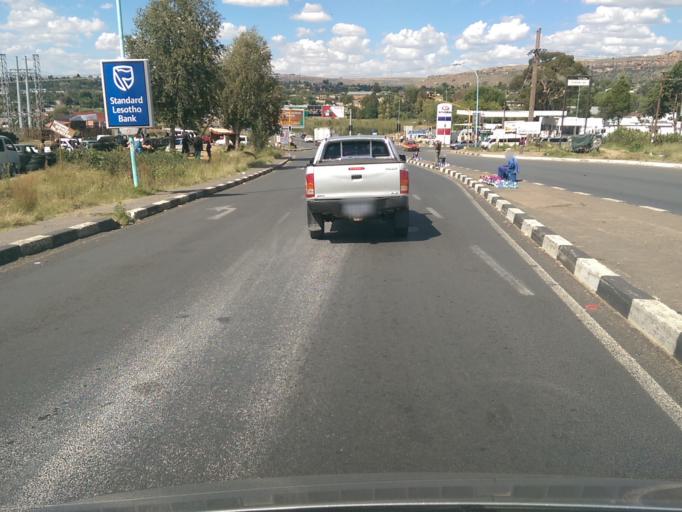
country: LS
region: Maseru
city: Maseru
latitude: -29.3130
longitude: 27.5089
